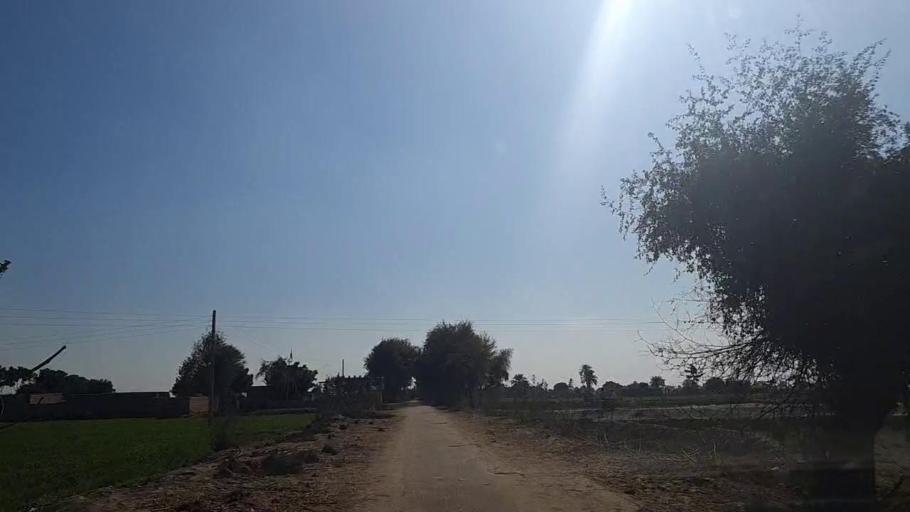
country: PK
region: Sindh
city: Sakrand
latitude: 26.2342
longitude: 68.1998
